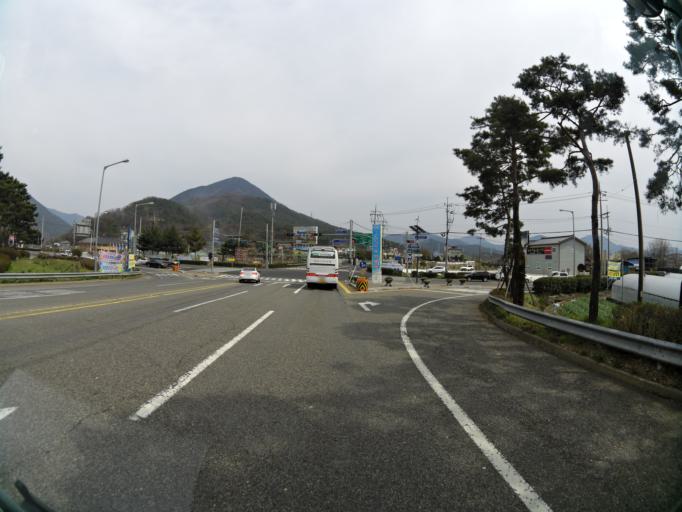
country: KR
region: Gyeongsangnam-do
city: Changnyeong
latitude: 35.4515
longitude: 128.5262
